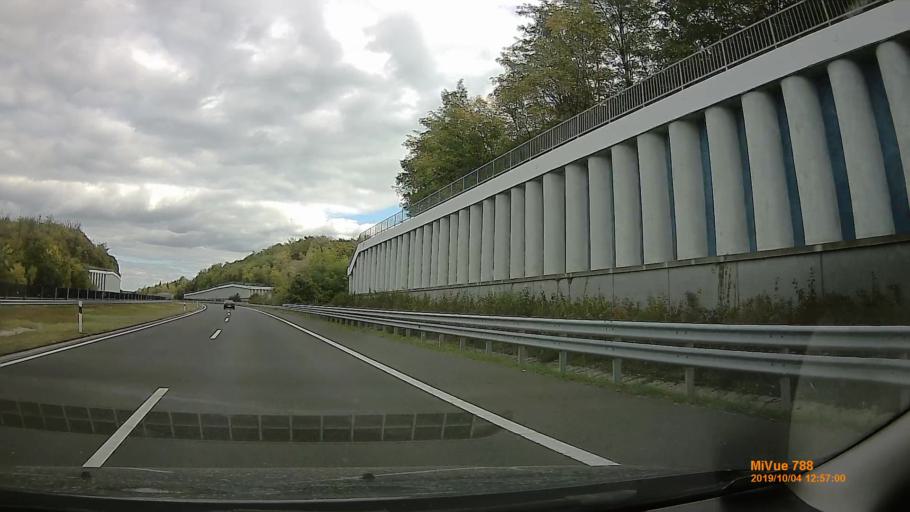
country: HU
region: Somogy
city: Balatonszarszo
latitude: 46.7900
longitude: 17.7907
